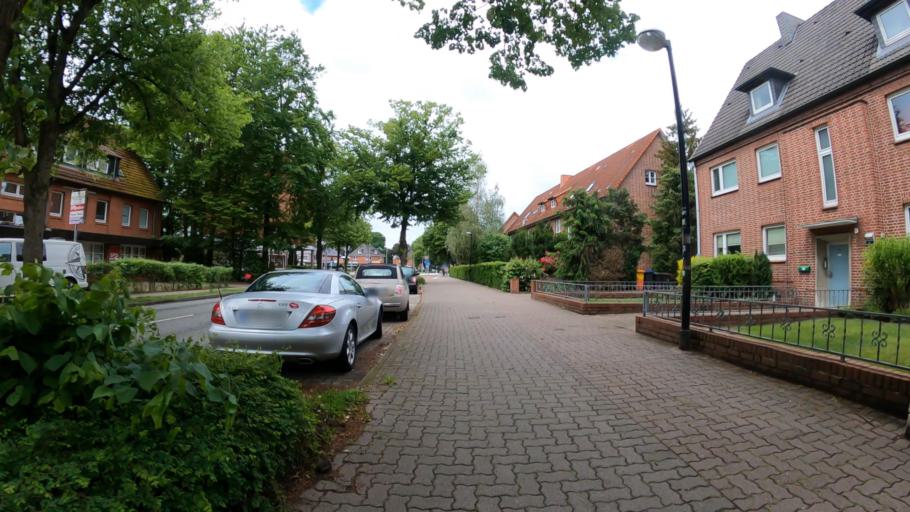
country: DE
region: Schleswig-Holstein
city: Norderstedt
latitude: 53.6821
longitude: 9.9829
